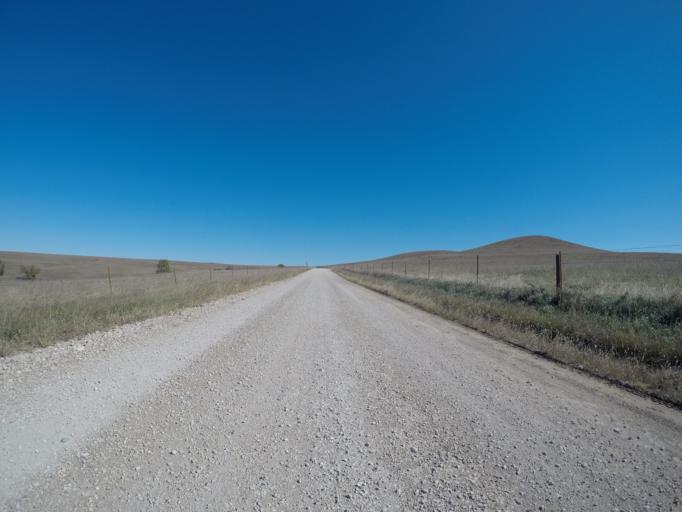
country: US
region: Kansas
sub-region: Wabaunsee County
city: Alma
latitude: 39.0105
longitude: -96.3972
